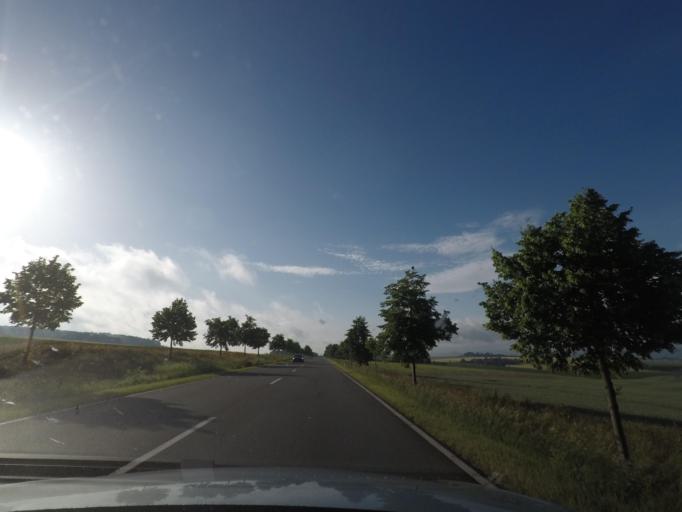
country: DE
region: Saxony-Anhalt
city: Huy-Neinstedt
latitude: 51.9494
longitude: 10.8854
